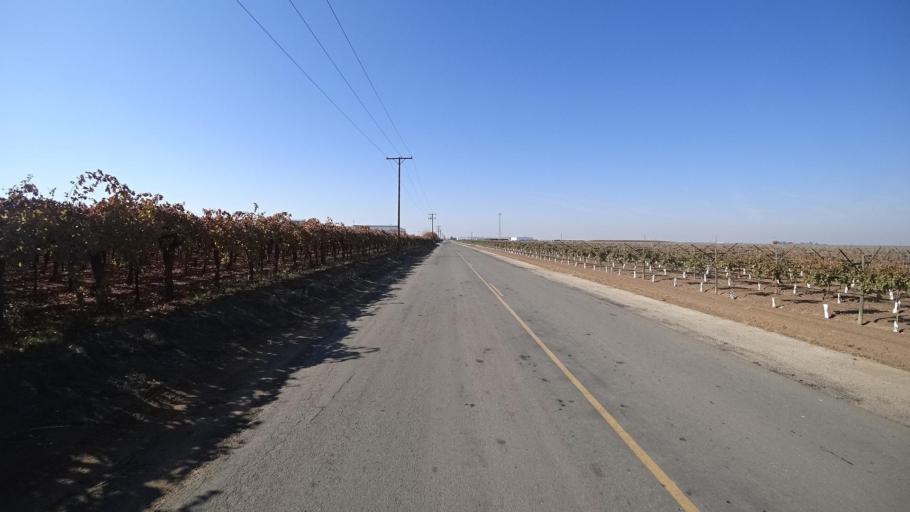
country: US
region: California
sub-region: Tulare County
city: Richgrove
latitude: 35.7180
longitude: -119.1478
